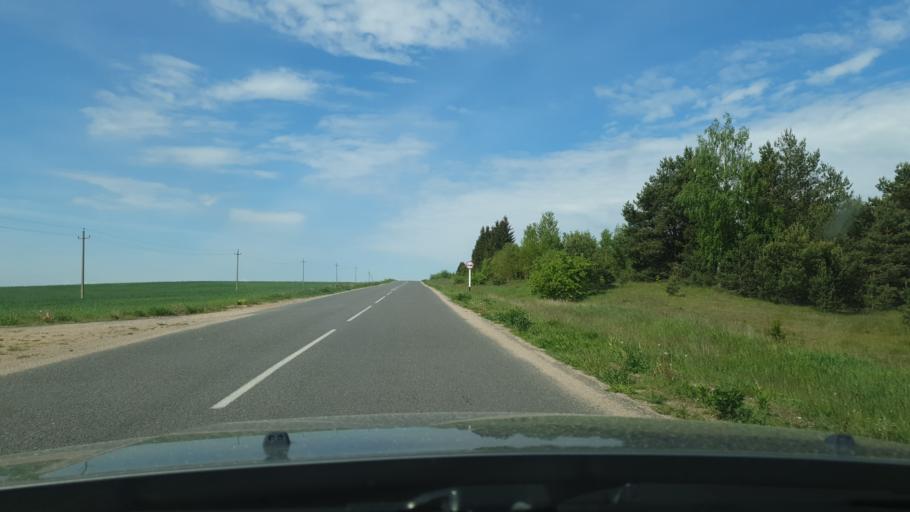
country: BY
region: Grodnenskaya
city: Mir
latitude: 53.4448
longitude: 26.4548
